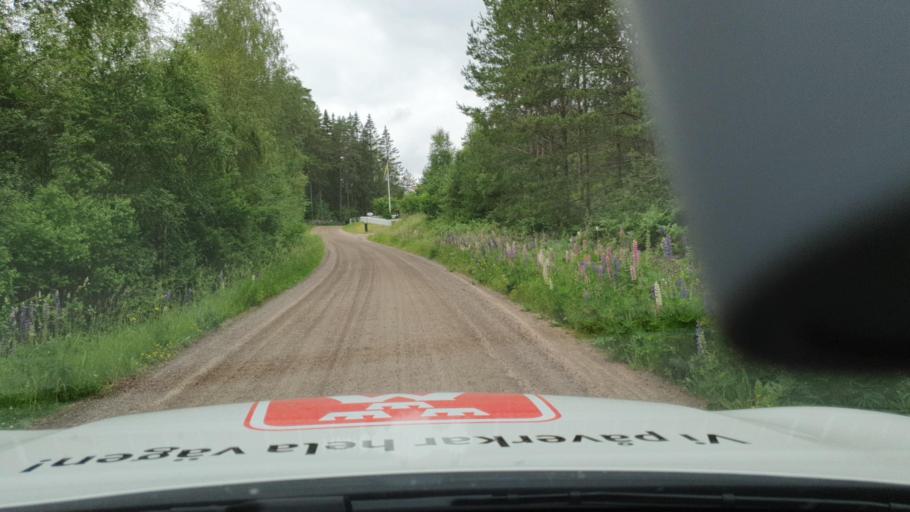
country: SE
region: Vaestra Goetaland
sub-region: Hjo Kommun
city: Hjo
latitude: 58.3391
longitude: 14.2719
